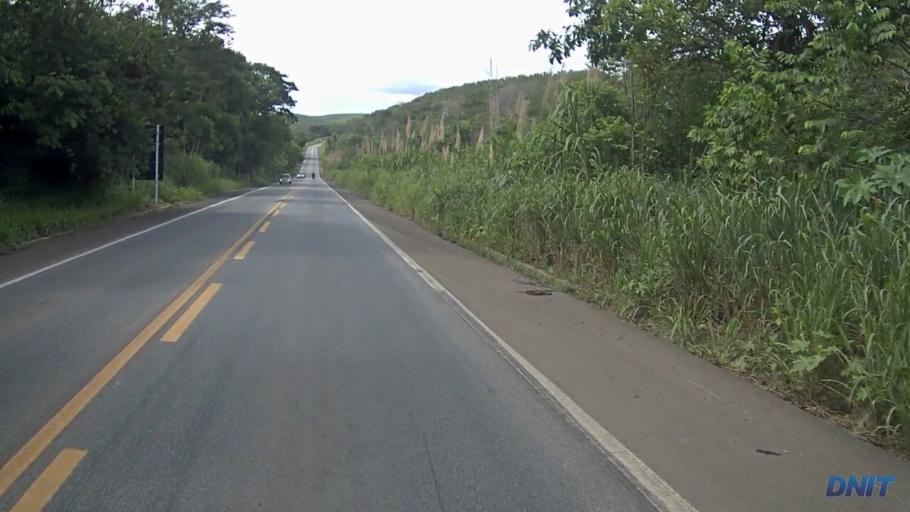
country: BR
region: Minas Gerais
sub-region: Ipaba
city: Ipaba
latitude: -19.3520
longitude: -42.4340
